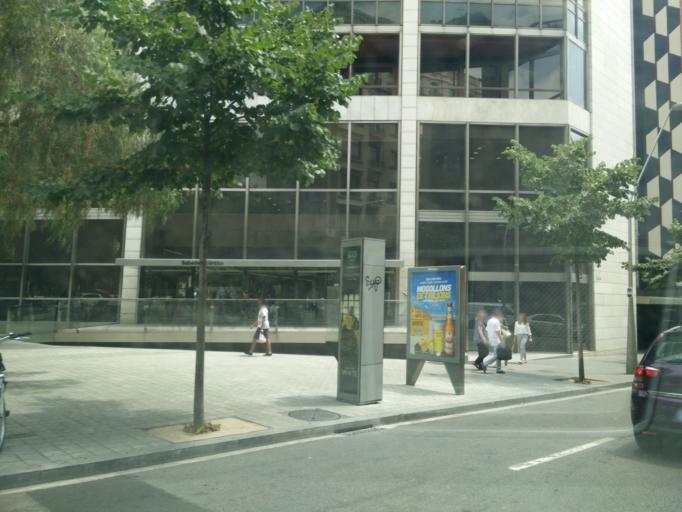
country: ES
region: Catalonia
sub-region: Provincia de Barcelona
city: Barcelona
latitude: 41.3950
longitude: 2.1552
